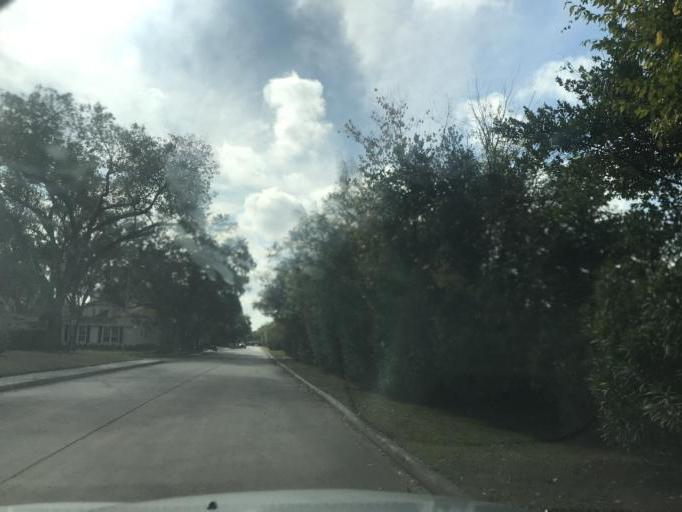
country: US
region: Texas
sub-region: Harris County
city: Hunters Creek Village
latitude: 29.7438
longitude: -95.4955
